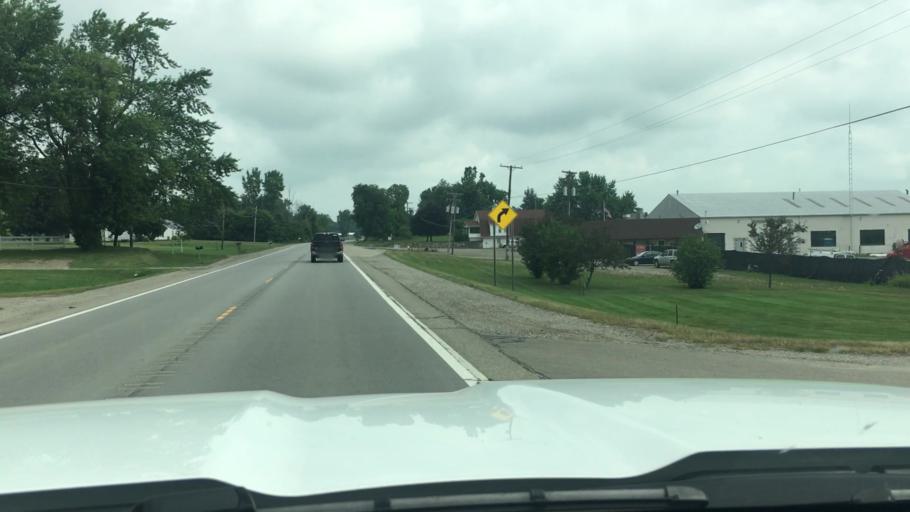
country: US
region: Michigan
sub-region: Lapeer County
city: Imlay City
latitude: 43.0452
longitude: -83.0724
